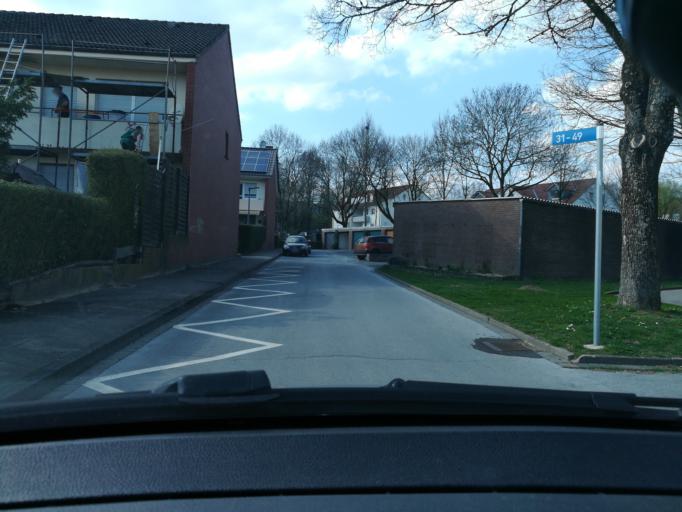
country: DE
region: North Rhine-Westphalia
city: Borgholzhausen
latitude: 52.1070
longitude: 8.3045
